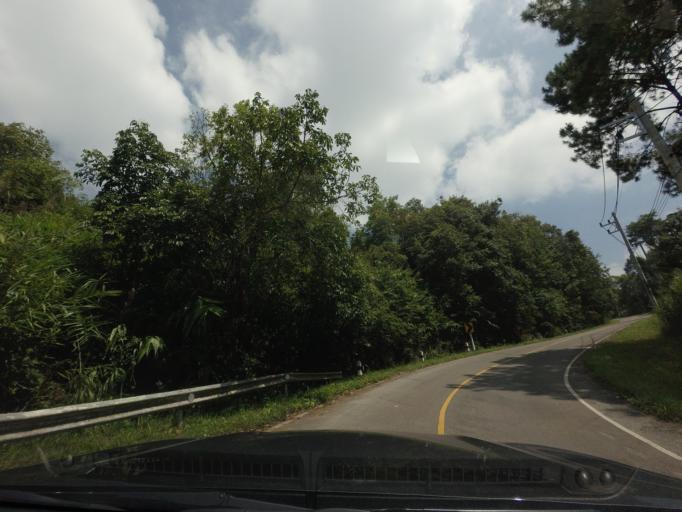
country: TH
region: Loei
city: Na Haeo
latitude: 17.4777
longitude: 100.9163
